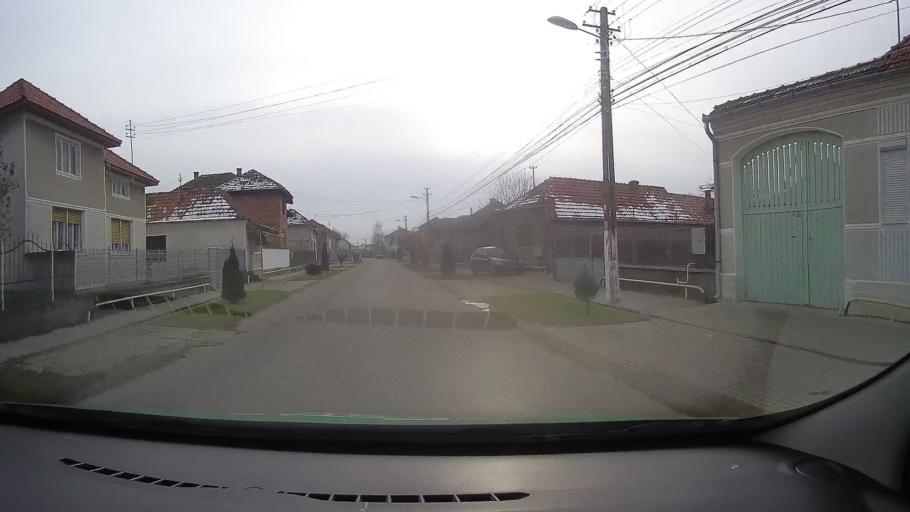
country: RO
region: Hunedoara
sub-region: Comuna Geoagiu
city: Geoagiu
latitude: 45.9295
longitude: 23.1962
